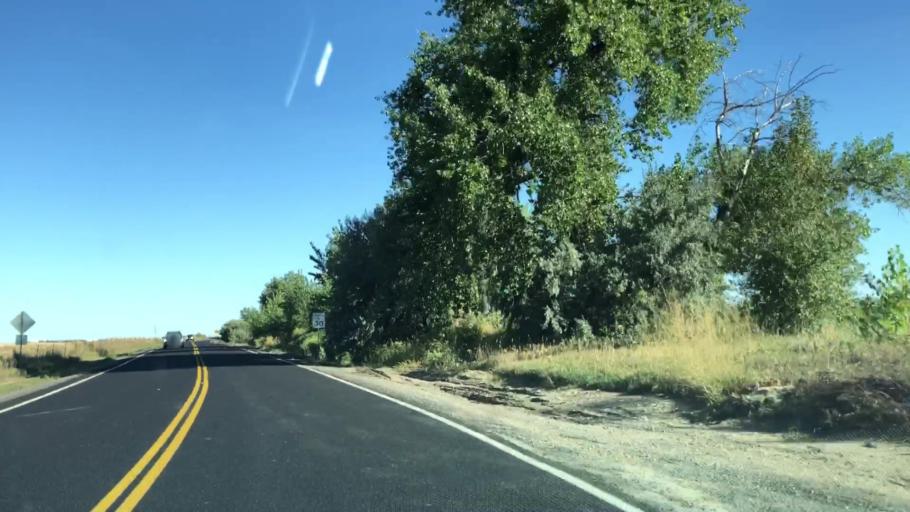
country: US
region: Colorado
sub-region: Larimer County
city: Loveland
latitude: 40.4646
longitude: -105.0530
